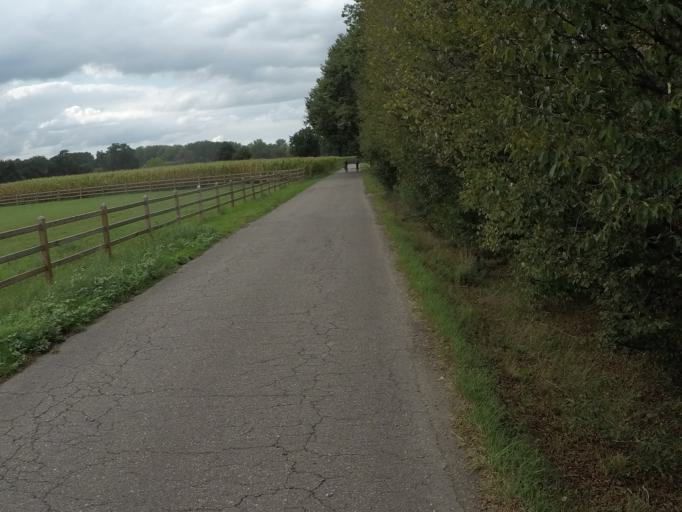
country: BE
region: Flanders
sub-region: Provincie Antwerpen
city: Zandhoven
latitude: 51.2022
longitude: 4.6952
